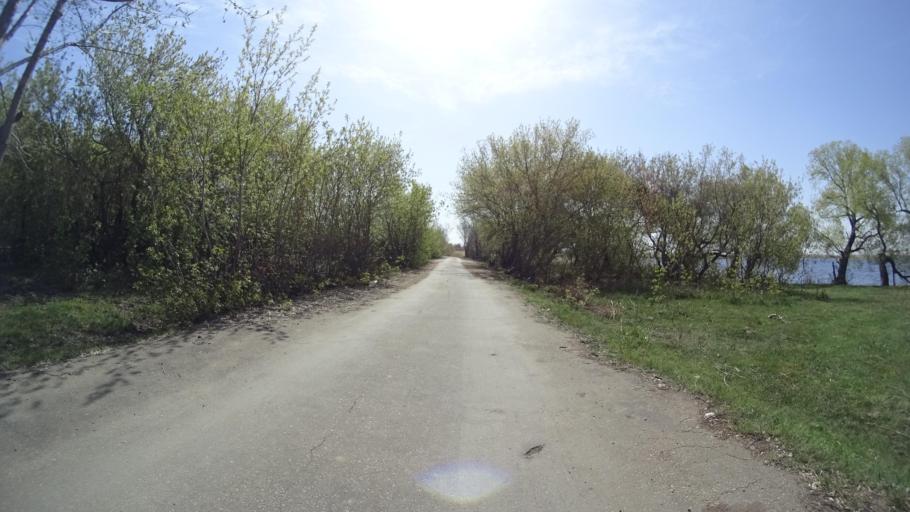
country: RU
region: Chelyabinsk
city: Chesma
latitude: 53.7972
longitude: 61.0241
